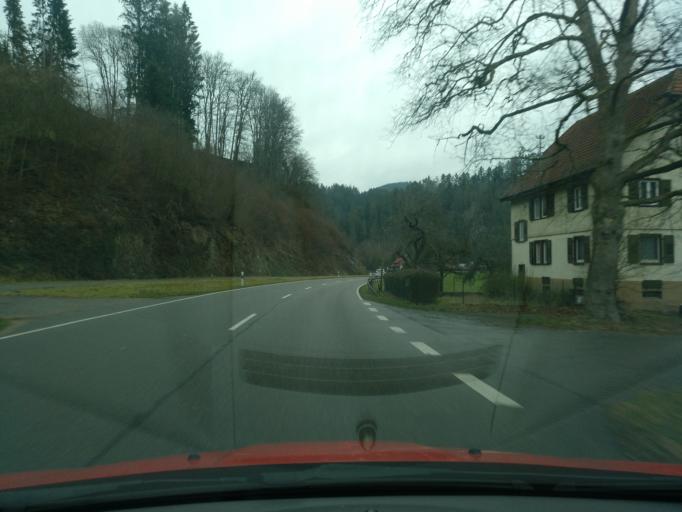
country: DE
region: Baden-Wuerttemberg
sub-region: Freiburg Region
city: Schramberg
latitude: 48.2572
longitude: 8.3721
